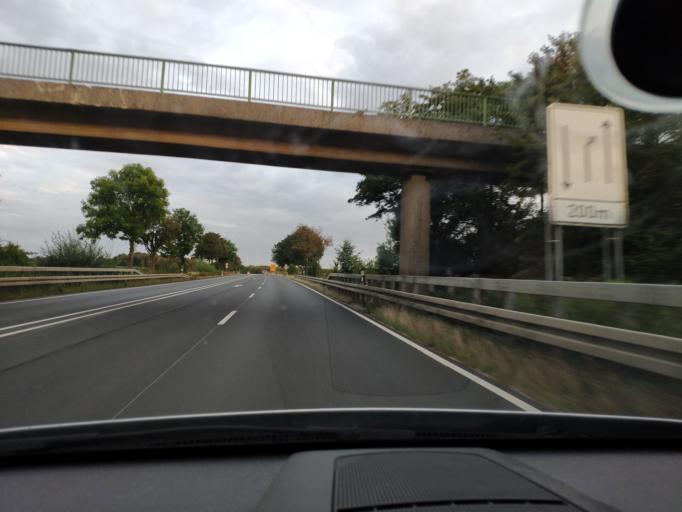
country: DE
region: North Rhine-Westphalia
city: Geilenkirchen
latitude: 50.9617
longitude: 6.0938
